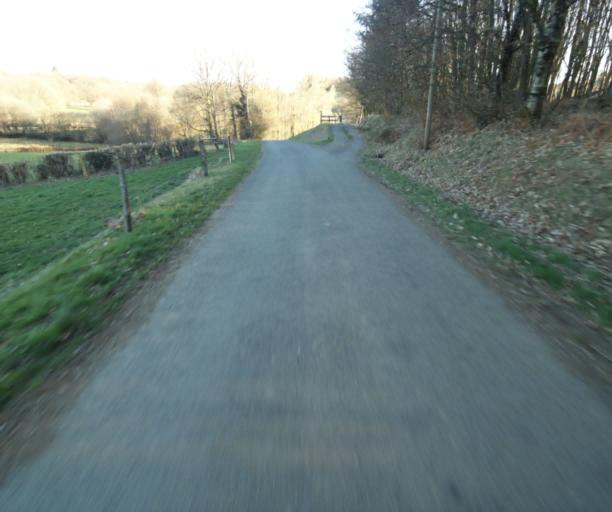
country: FR
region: Limousin
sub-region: Departement de la Correze
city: Seilhac
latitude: 45.3583
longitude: 1.7002
